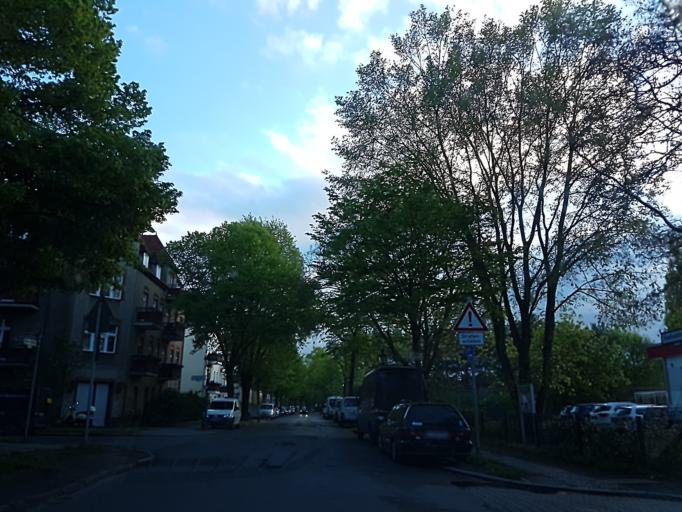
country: DE
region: Berlin
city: Hermsdorf
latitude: 52.6159
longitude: 13.3231
